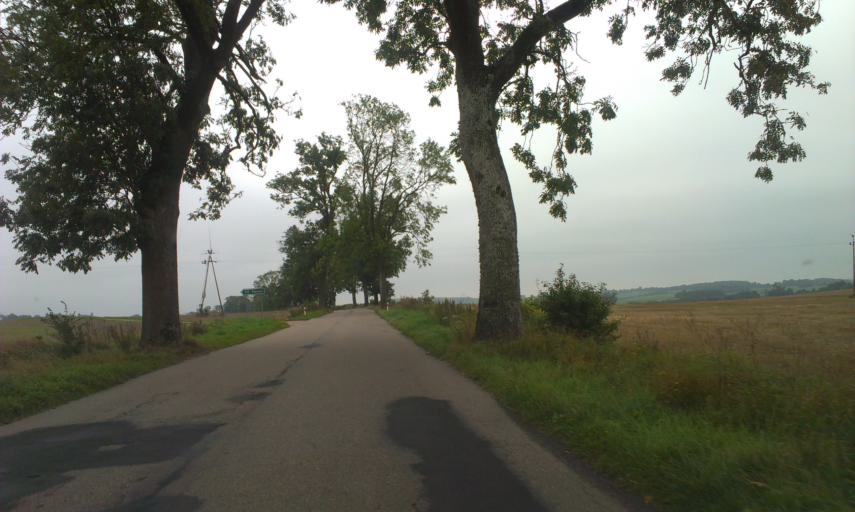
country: PL
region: West Pomeranian Voivodeship
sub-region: Powiat szczecinecki
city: Barwice
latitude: 53.7264
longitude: 16.3546
